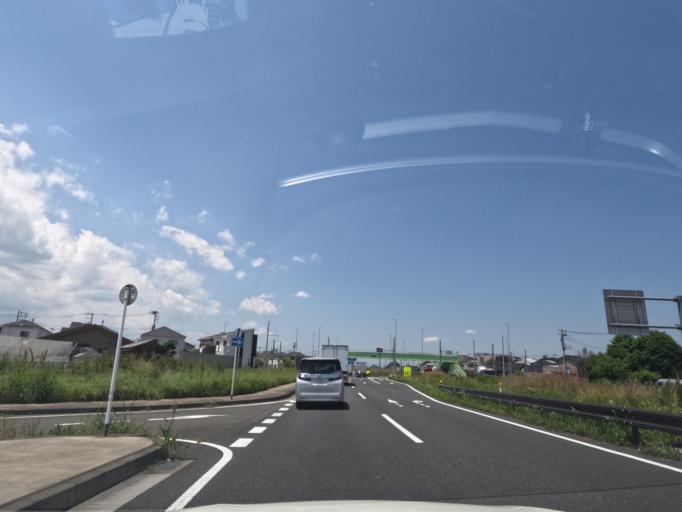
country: JP
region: Saitama
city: Okegawa
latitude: 35.9609
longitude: 139.5617
